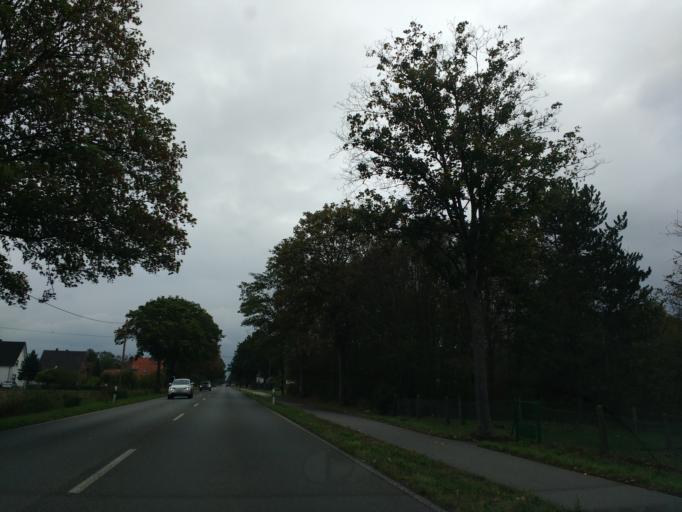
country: DE
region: North Rhine-Westphalia
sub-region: Regierungsbezirk Dusseldorf
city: Alpen
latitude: 51.5979
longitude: 6.5307
